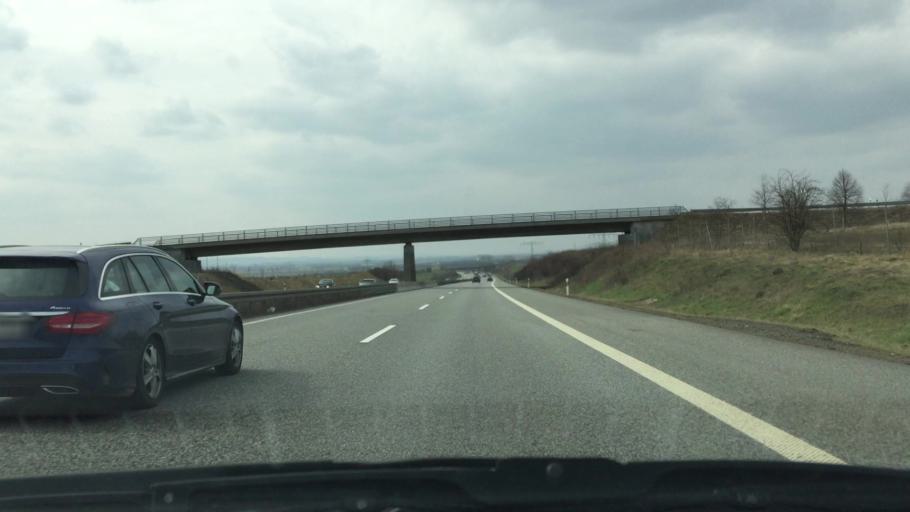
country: DE
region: Thuringia
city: Gorsbach
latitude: 51.4684
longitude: 10.9515
